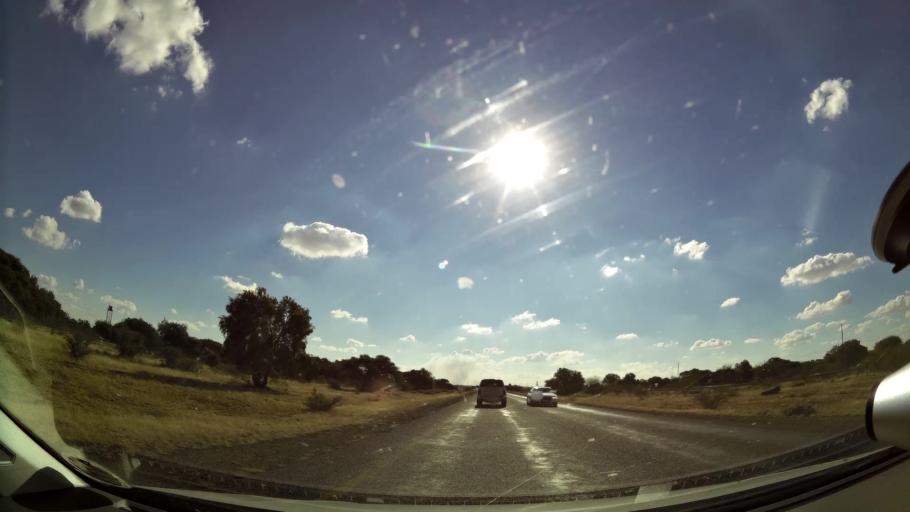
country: ZA
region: Northern Cape
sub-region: Frances Baard District Municipality
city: Kimberley
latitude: -28.7903
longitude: 24.7842
